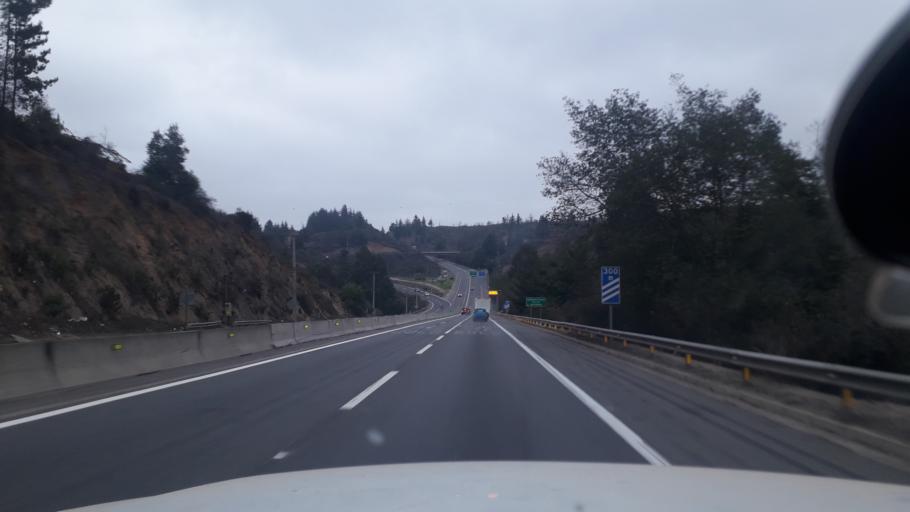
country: CL
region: Valparaiso
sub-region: Provincia de Valparaiso
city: Vina del Mar
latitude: -33.0832
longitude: -71.5460
